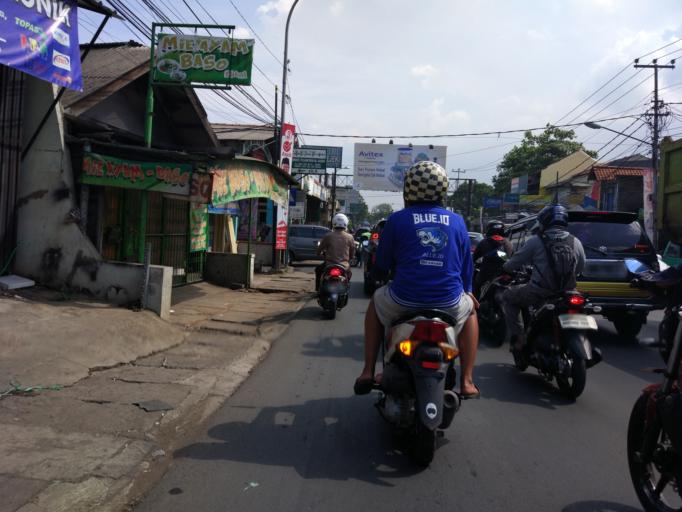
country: ID
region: West Java
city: Cileunyi
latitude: -6.9335
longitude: 107.7232
